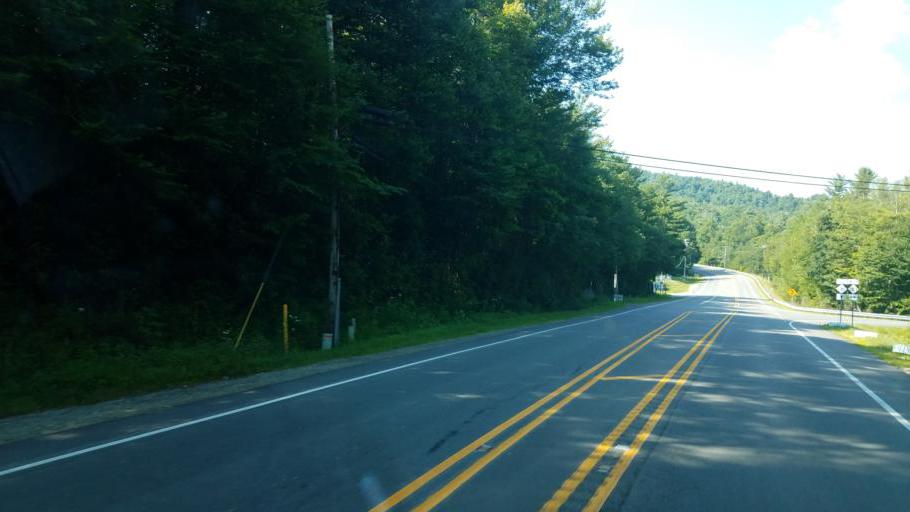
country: US
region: North Carolina
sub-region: Avery County
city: Newland
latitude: 35.9844
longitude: -81.8953
